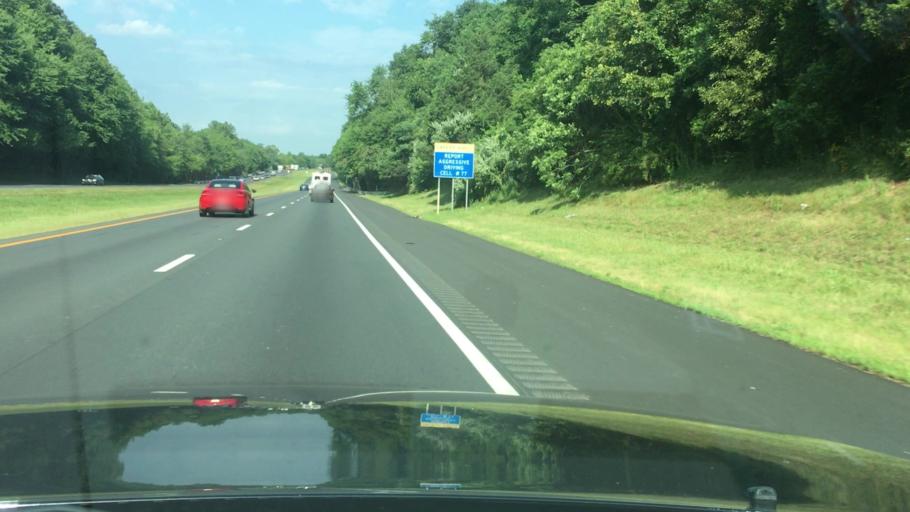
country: US
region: New Jersey
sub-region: Monmouth County
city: Shrewsbury
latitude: 40.1743
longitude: -74.4783
